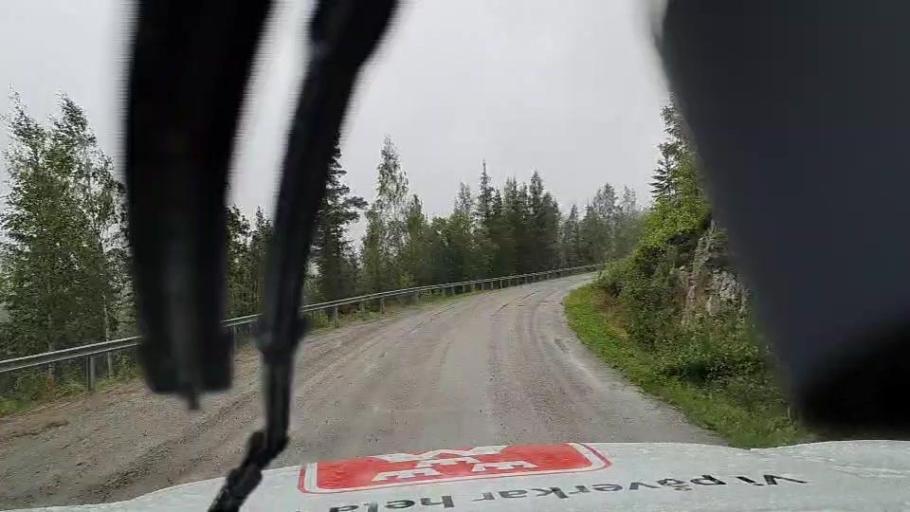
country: SE
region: Jaemtland
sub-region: OEstersunds Kommun
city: Brunflo
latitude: 62.8238
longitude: 15.0215
